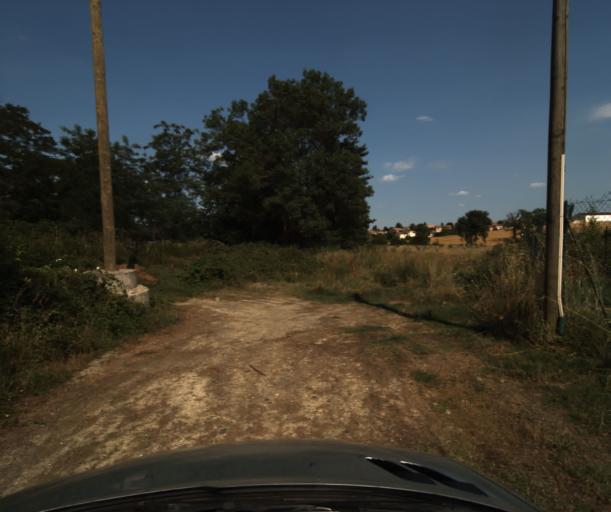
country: FR
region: Midi-Pyrenees
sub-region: Departement de la Haute-Garonne
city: Saint-Lys
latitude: 43.5164
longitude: 1.1810
